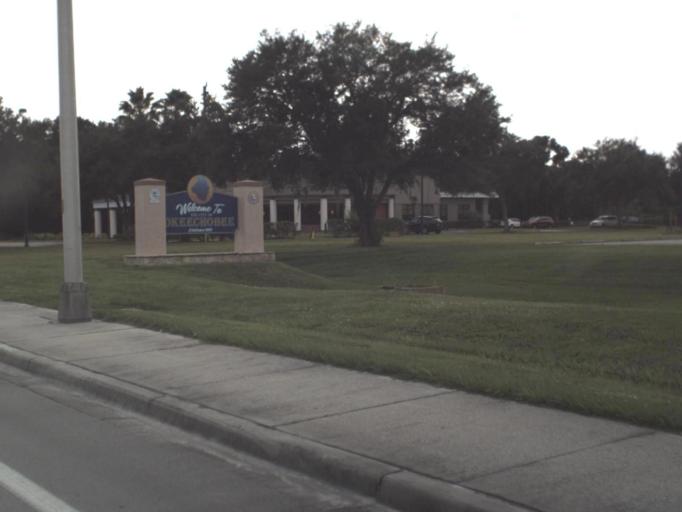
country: US
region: Florida
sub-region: Okeechobee County
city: Okeechobee
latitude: 27.2595
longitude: -80.8300
